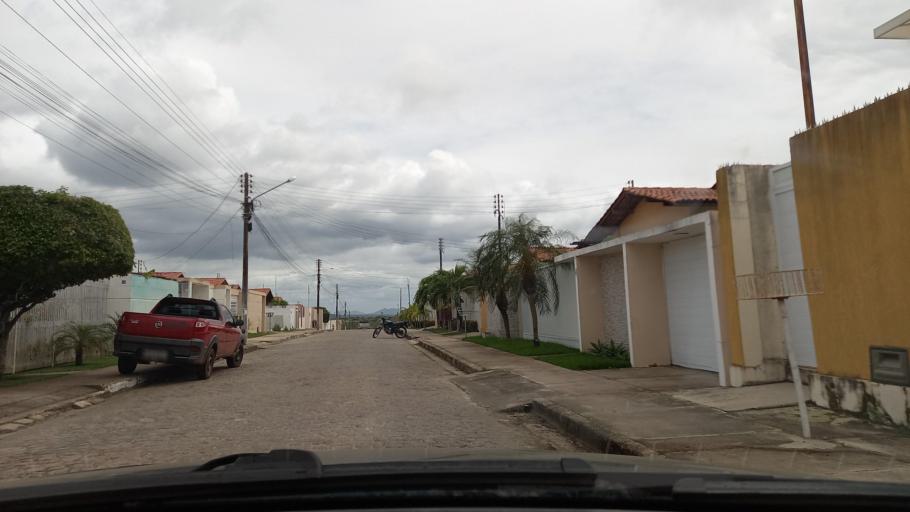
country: BR
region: Sergipe
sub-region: Caninde De Sao Francisco
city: Caninde de Sao Francisco
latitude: -9.6132
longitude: -37.7636
